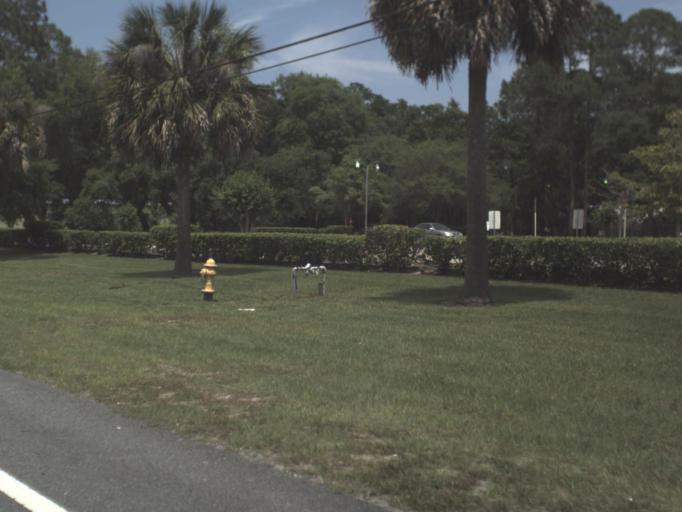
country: US
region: Florida
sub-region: Nassau County
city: Yulee
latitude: 30.4868
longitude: -81.6262
